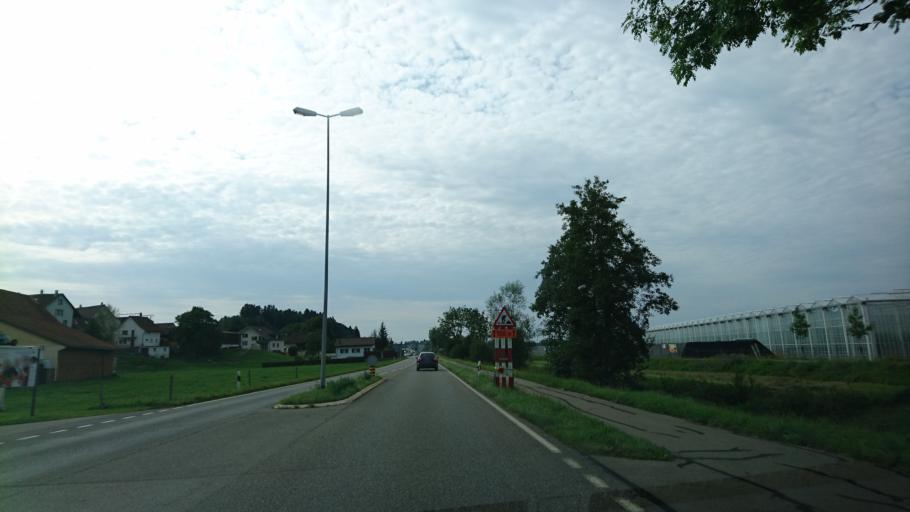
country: CH
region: Zurich
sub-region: Bezirk Hinwil
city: Wetzikon / Ober-Wetzikon
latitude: 47.3078
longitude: 8.8170
